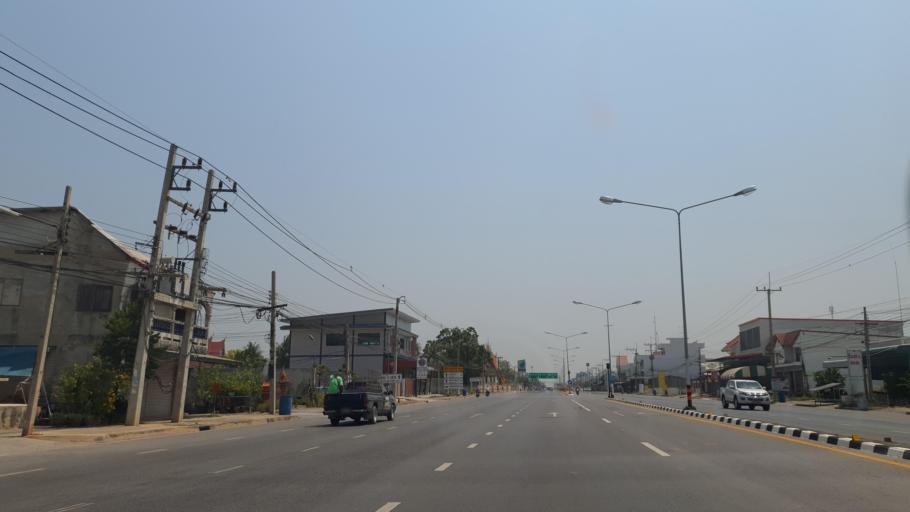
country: TH
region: Suphan Buri
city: U Thong
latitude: 14.2505
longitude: 99.8161
